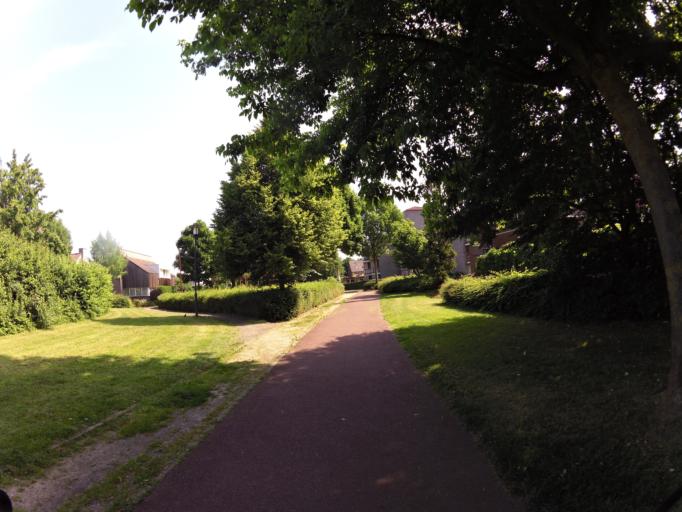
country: NL
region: Limburg
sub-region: Gemeente Kerkrade
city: Kerkrade
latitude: 50.9184
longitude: 6.0379
